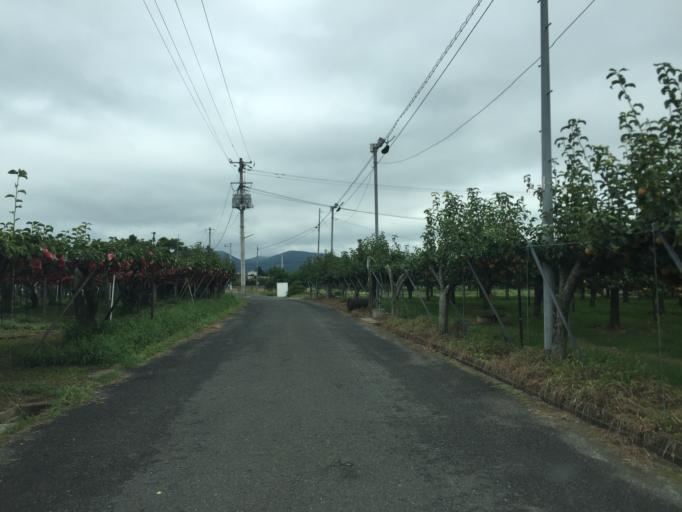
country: JP
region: Fukushima
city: Fukushima-shi
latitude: 37.7671
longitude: 140.4083
